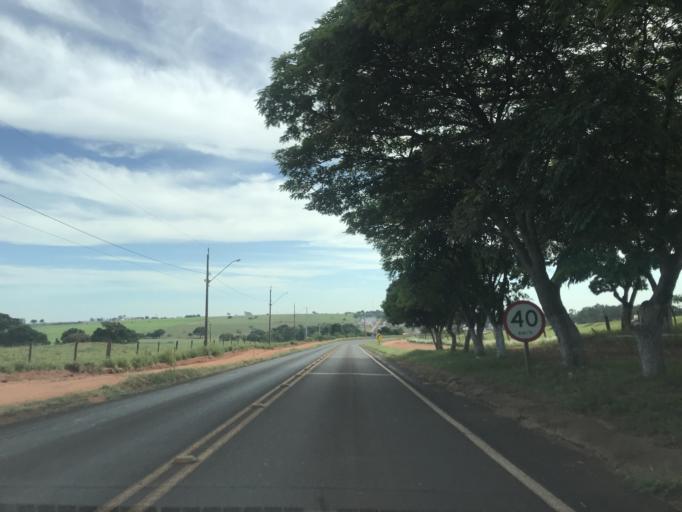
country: BR
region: Parana
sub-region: Paranavai
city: Nova Aurora
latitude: -22.9449
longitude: -52.6966
